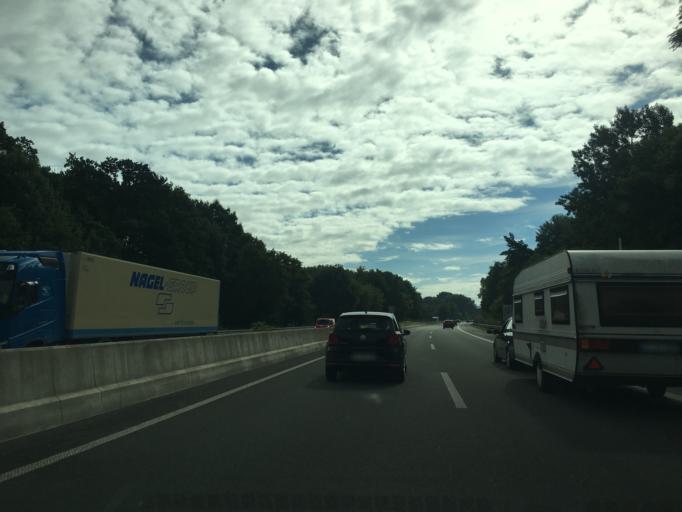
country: DE
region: North Rhine-Westphalia
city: Loehne
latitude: 52.2077
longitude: 8.7230
